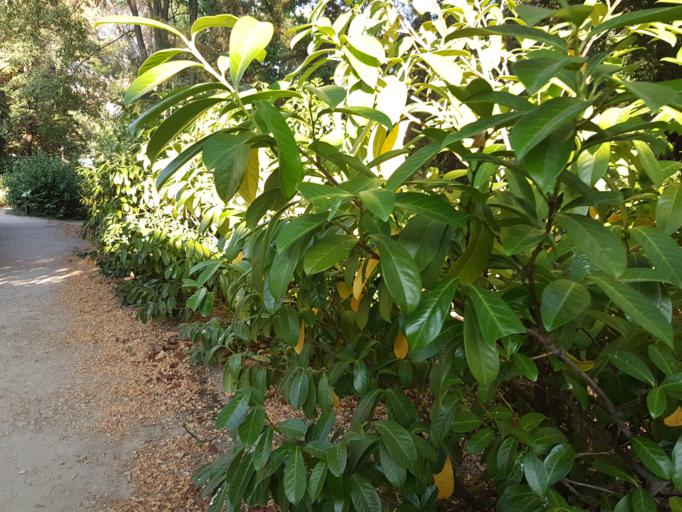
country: ES
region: Madrid
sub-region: Provincia de Madrid
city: Tetuan de las Victorias
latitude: 40.4502
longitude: -3.7209
